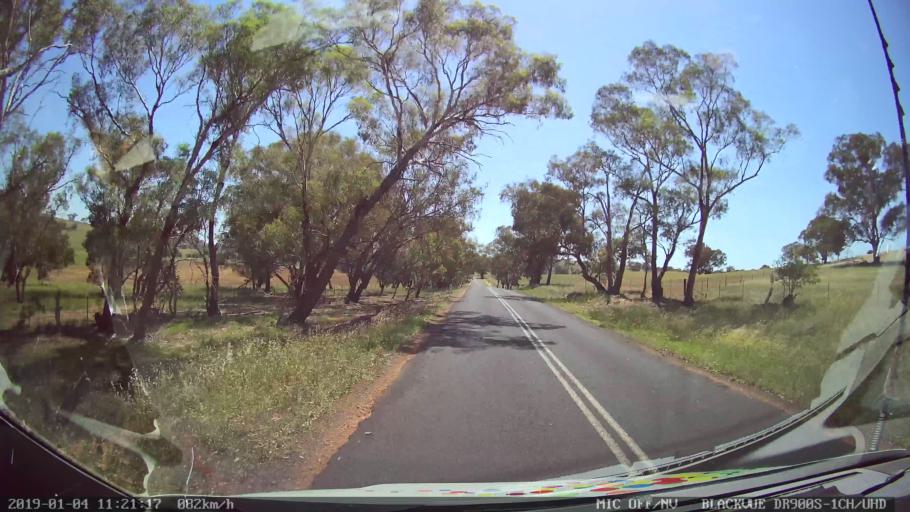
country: AU
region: New South Wales
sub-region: Cabonne
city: Molong
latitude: -33.1556
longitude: 148.7091
